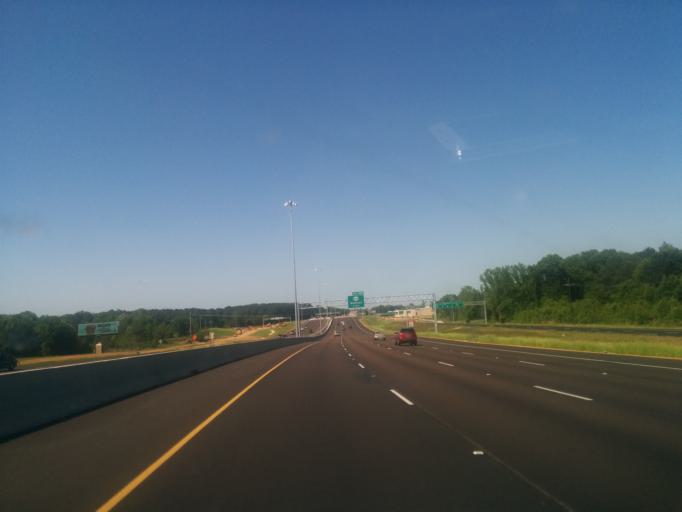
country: US
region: Mississippi
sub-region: Madison County
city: Ridgeland
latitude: 32.4518
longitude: -90.1444
